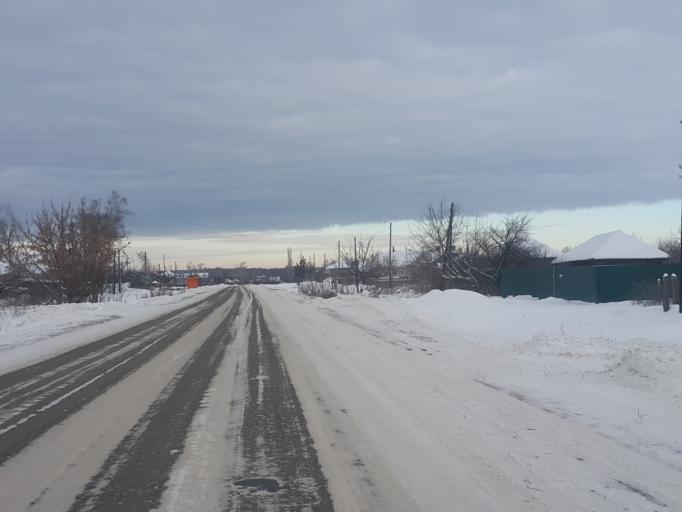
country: RU
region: Tambov
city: Platonovka
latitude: 52.8388
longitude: 41.8132
